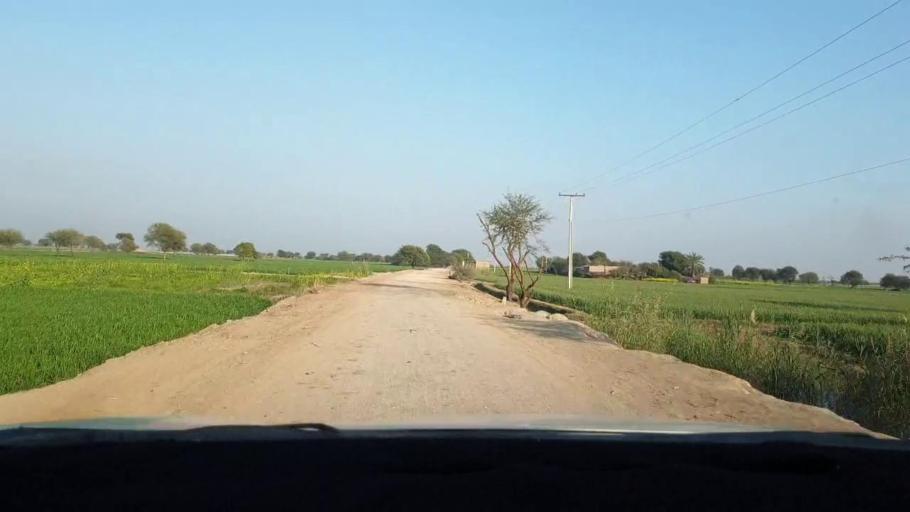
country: PK
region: Sindh
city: Berani
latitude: 25.7460
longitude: 68.7406
